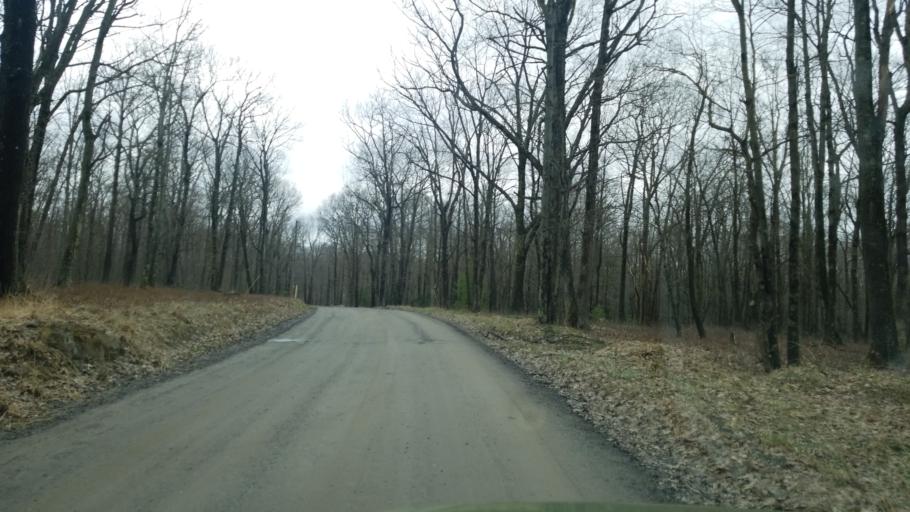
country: US
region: Pennsylvania
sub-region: Clearfield County
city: Shiloh
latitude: 41.1782
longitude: -78.3252
